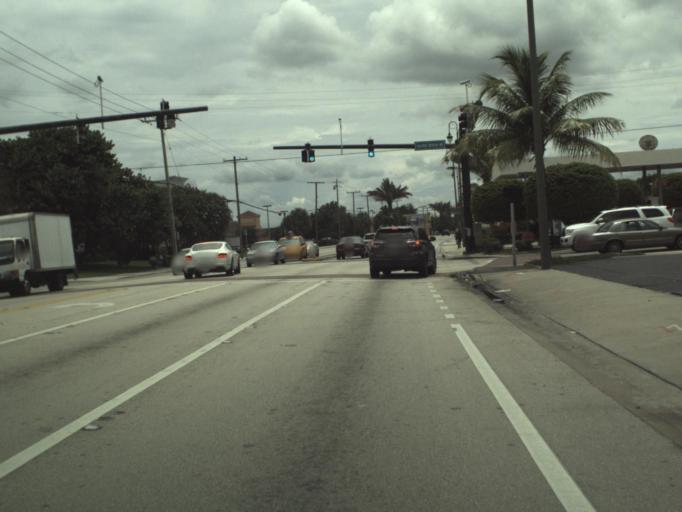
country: US
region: Florida
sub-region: Palm Beach County
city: Lake Park
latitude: 26.7930
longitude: -80.0543
